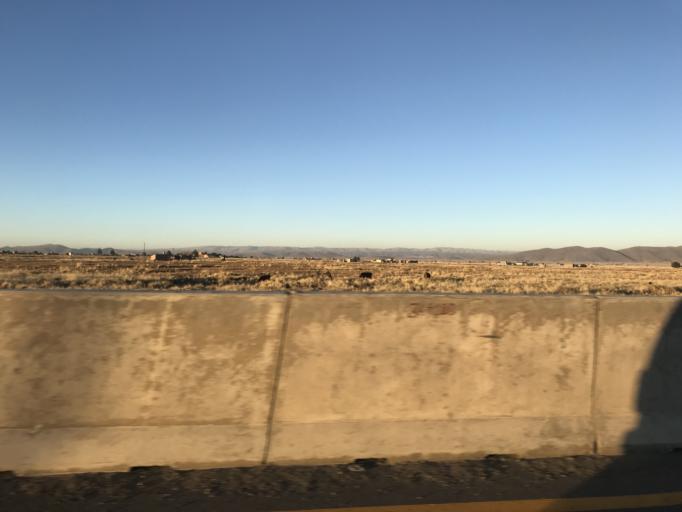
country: BO
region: La Paz
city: Batallas
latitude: -16.3073
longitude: -68.4708
